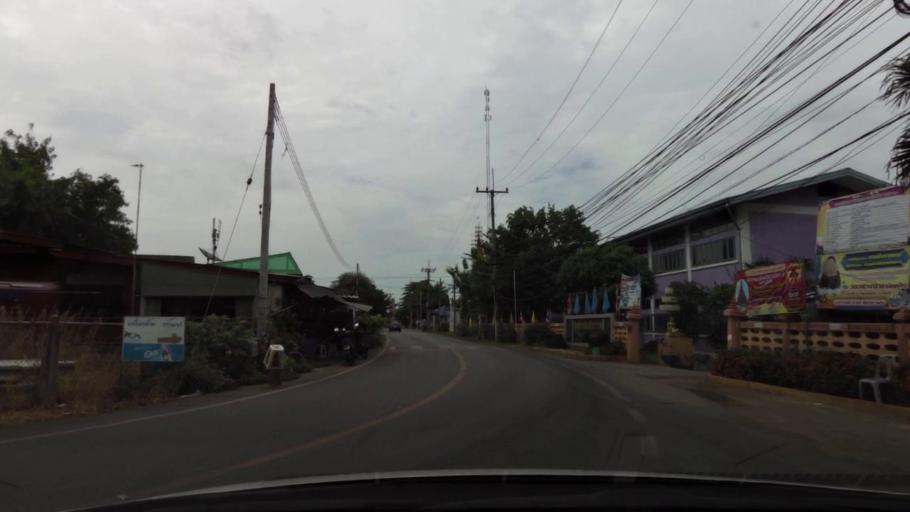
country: TH
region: Ratchaburi
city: Damnoen Saduak
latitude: 13.5755
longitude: 100.0033
